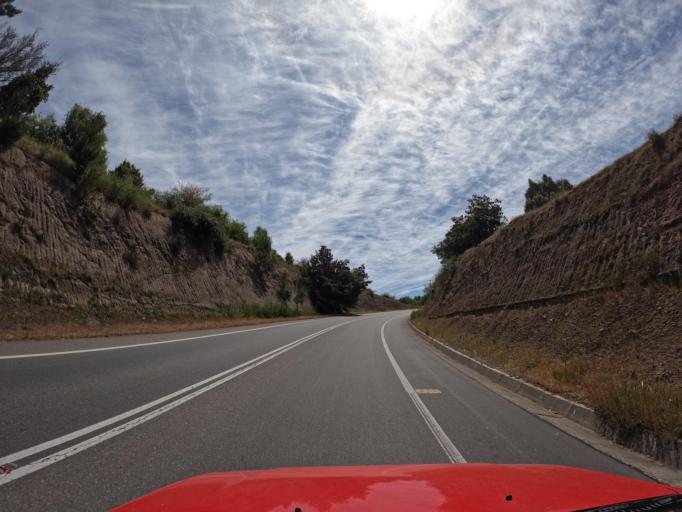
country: CL
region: Maule
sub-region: Provincia de Talca
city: Talca
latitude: -35.2782
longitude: -71.5376
